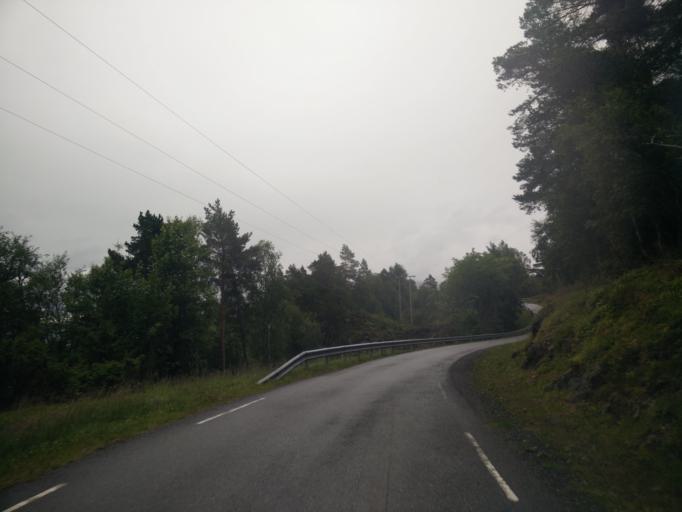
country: NO
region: More og Romsdal
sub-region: Kristiansund
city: Rensvik
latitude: 63.0366
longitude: 7.9151
